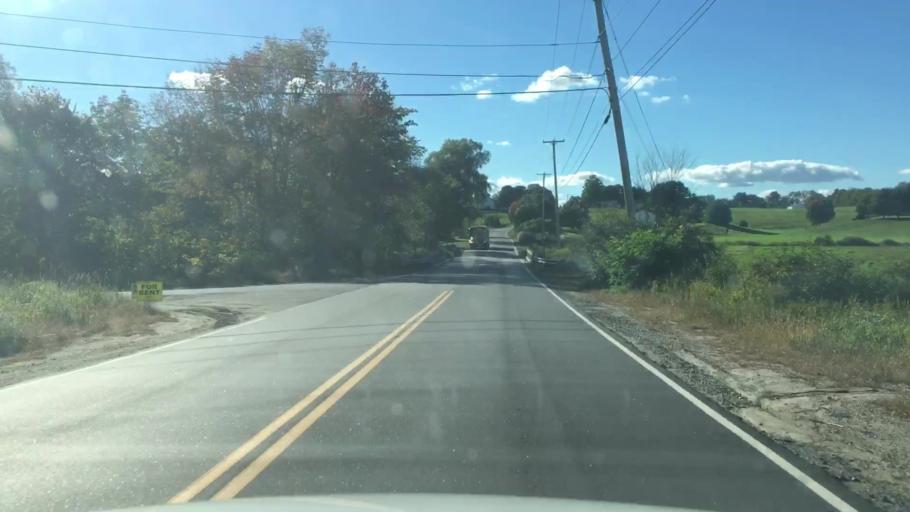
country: US
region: Maine
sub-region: Androscoggin County
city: Lisbon
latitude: 44.0749
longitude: -70.1035
